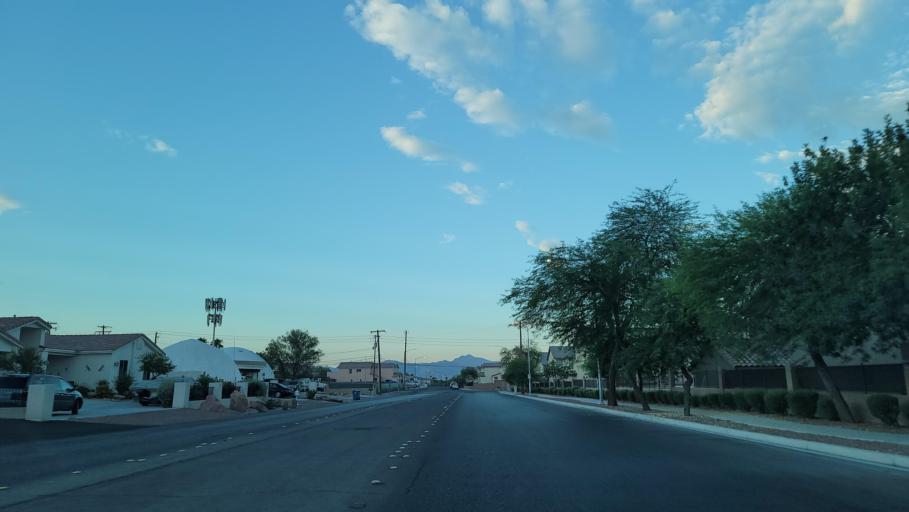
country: US
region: Nevada
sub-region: Clark County
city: Sunrise Manor
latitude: 36.1612
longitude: -115.0354
